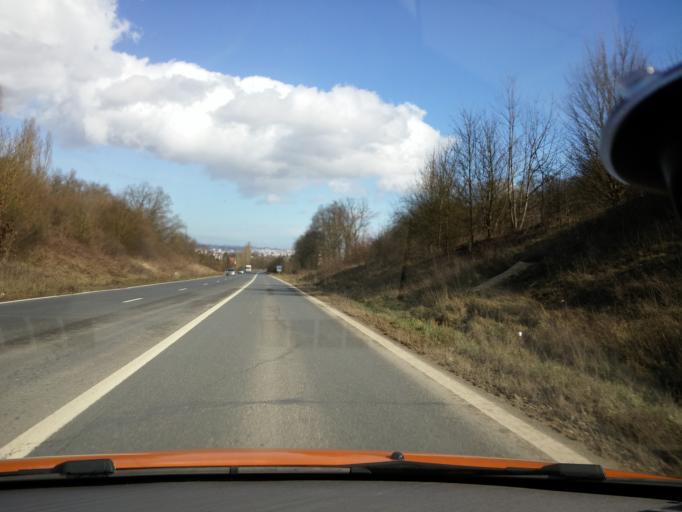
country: FR
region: Ile-de-France
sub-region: Departement de l'Essonne
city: Villebon-sur-Yvette
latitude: 48.7220
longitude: 2.2326
